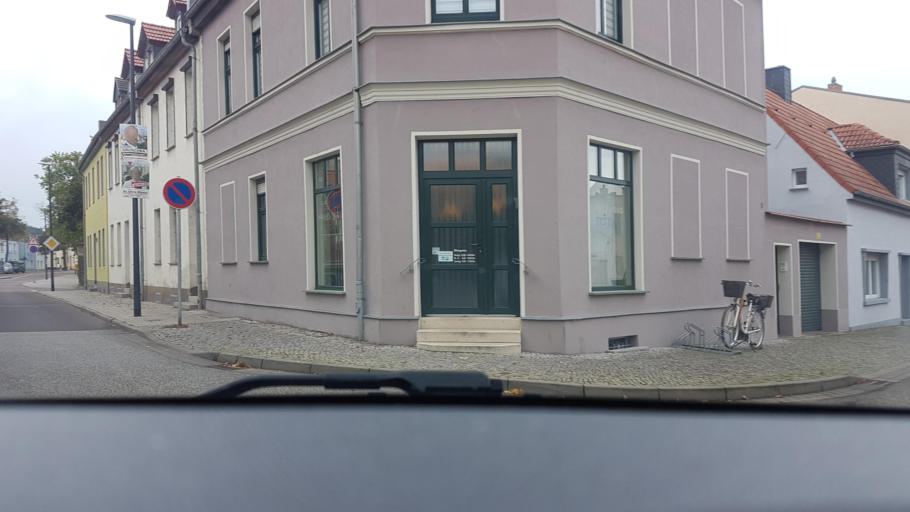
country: DE
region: Saxony-Anhalt
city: Bernburg
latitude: 51.7918
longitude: 11.7385
